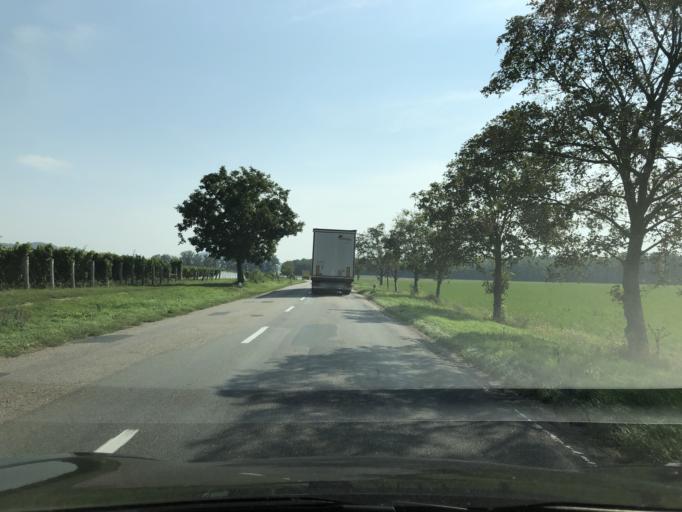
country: CZ
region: South Moravian
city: Brezi
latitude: 48.8190
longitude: 16.5839
